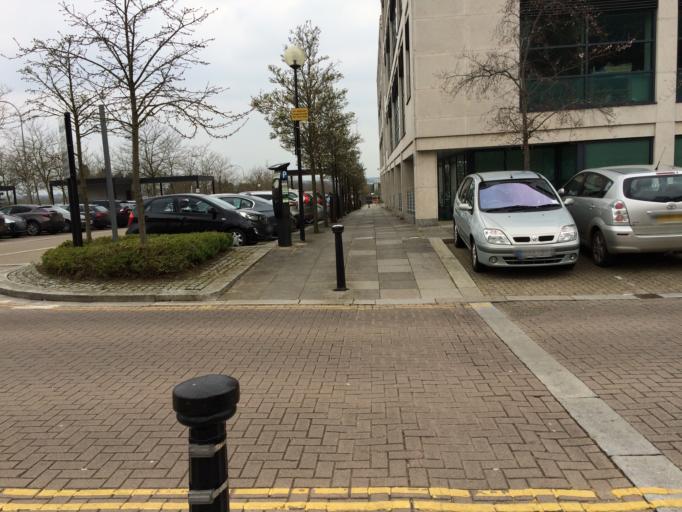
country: GB
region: England
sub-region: Milton Keynes
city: Milton Keynes
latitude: 52.0363
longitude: -0.7647
